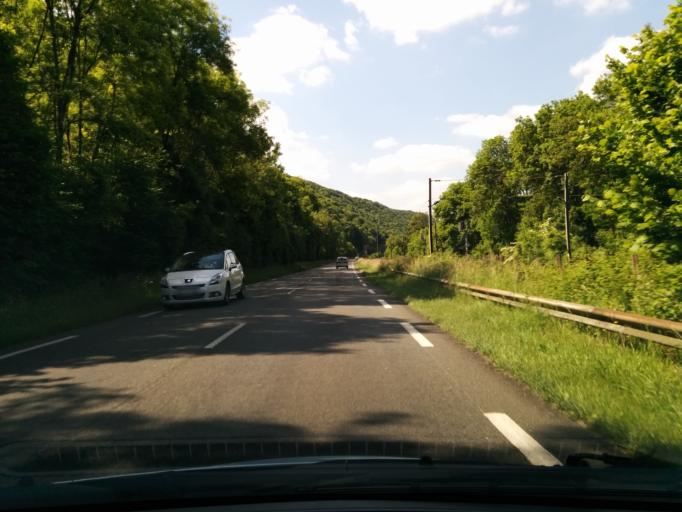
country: FR
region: Ile-de-France
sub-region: Departement des Yvelines
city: Bennecourt
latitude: 49.0410
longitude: 1.5358
